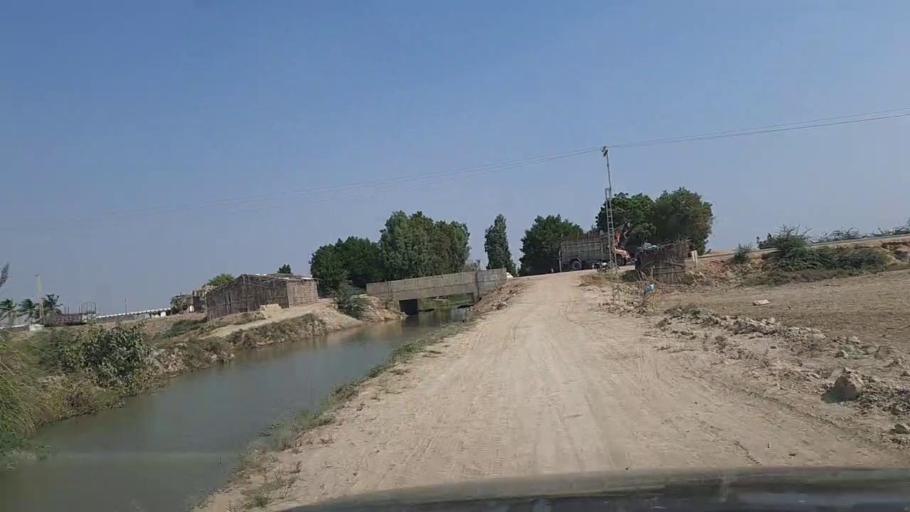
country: PK
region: Sindh
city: Gharo
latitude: 24.7142
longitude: 67.5915
